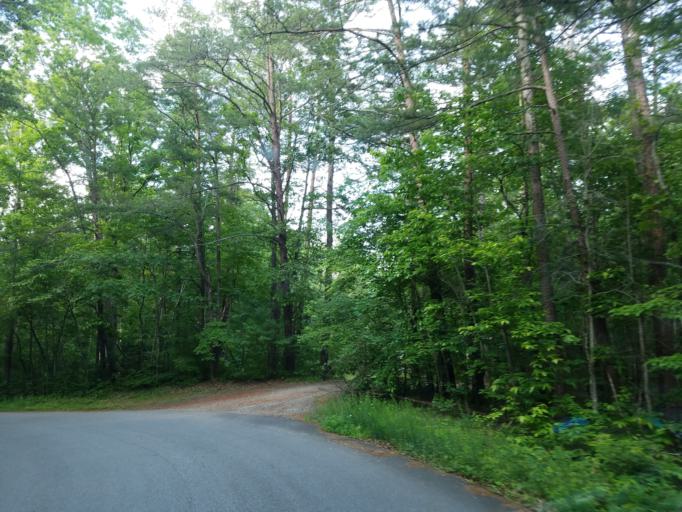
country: US
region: Georgia
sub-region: Lumpkin County
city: Dahlonega
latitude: 34.5555
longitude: -84.0752
